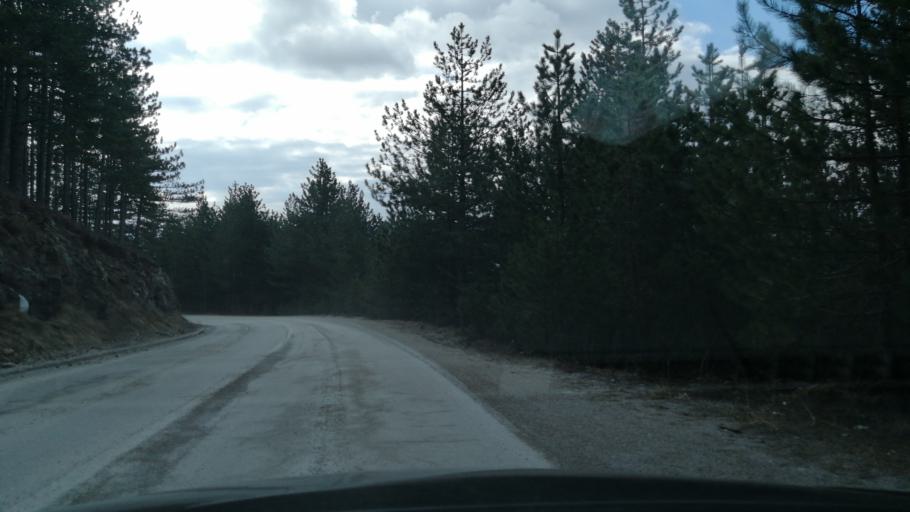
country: RS
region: Central Serbia
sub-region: Zlatiborski Okrug
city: Bajina Basta
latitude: 43.8721
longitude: 19.5697
